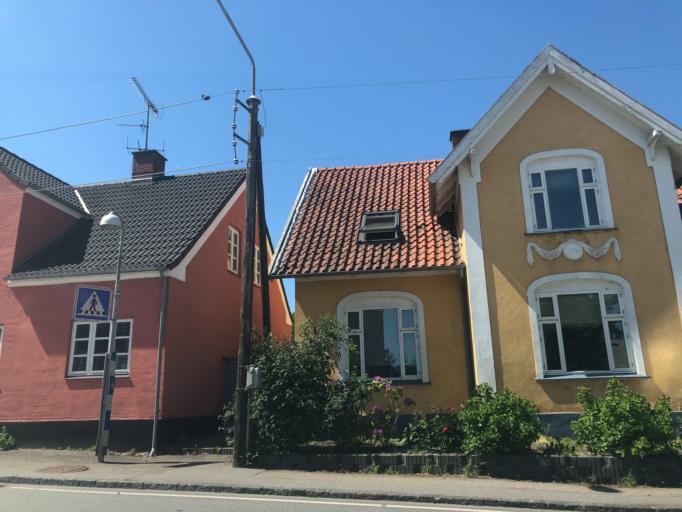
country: DK
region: Capital Region
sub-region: Gribskov Kommune
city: Graested
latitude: 56.0673
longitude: 12.2817
